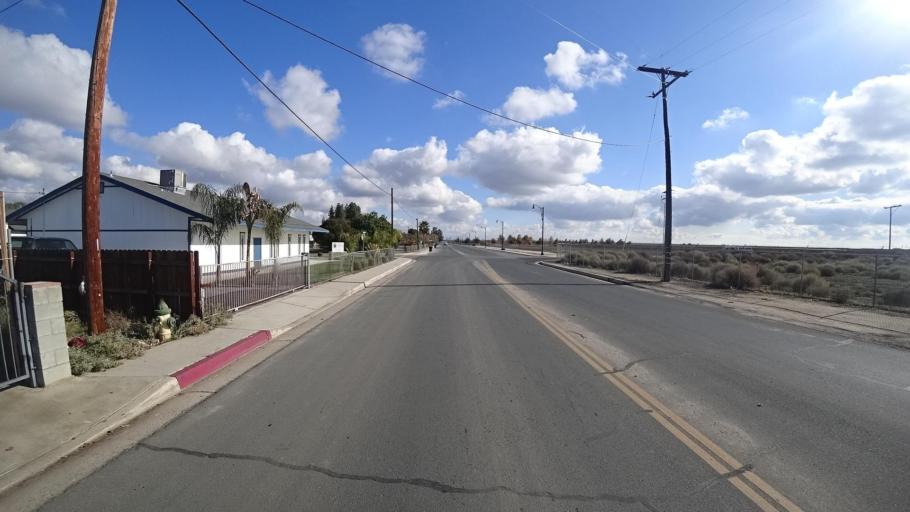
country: US
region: California
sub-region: Kern County
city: McFarland
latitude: 35.6746
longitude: -119.2237
